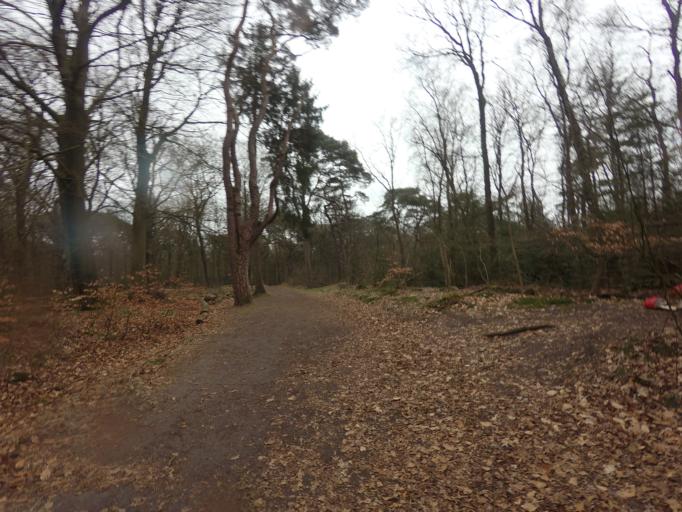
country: NL
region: Friesland
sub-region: Gemeente Gaasterlan-Sleat
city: Oudemirdum
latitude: 52.8589
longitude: 5.4943
